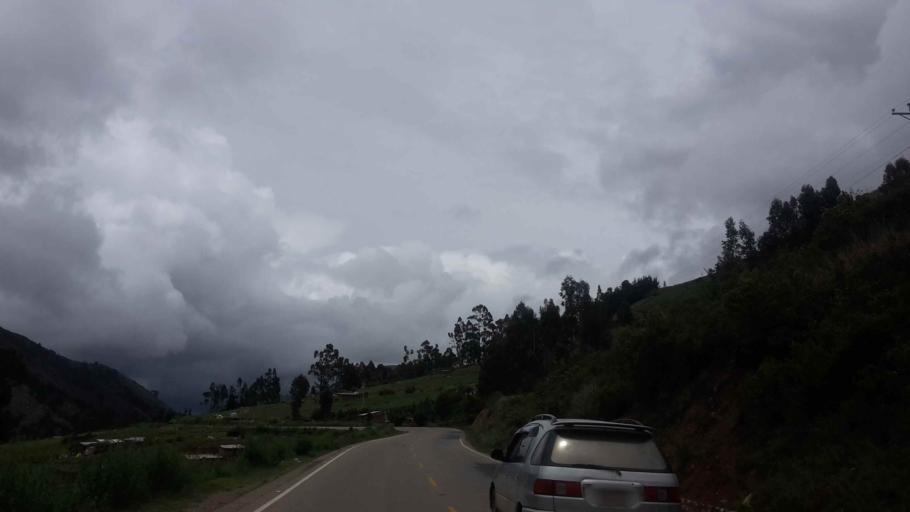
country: BO
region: Cochabamba
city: Arani
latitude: -17.4771
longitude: -65.4955
